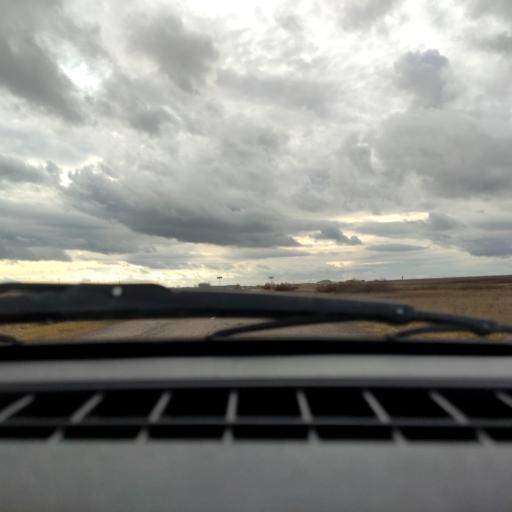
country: RU
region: Bashkortostan
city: Asanovo
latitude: 54.9217
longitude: 55.5112
